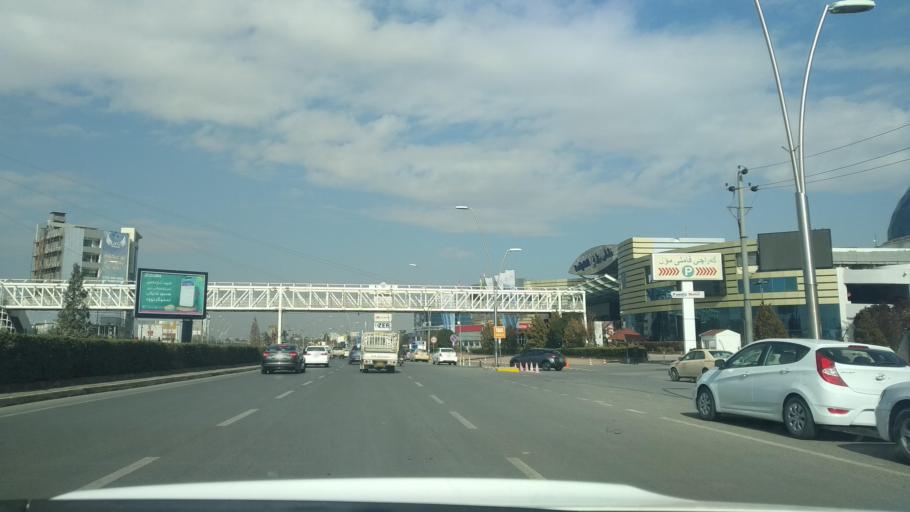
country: IQ
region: Arbil
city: Erbil
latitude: 36.2085
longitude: 44.0445
